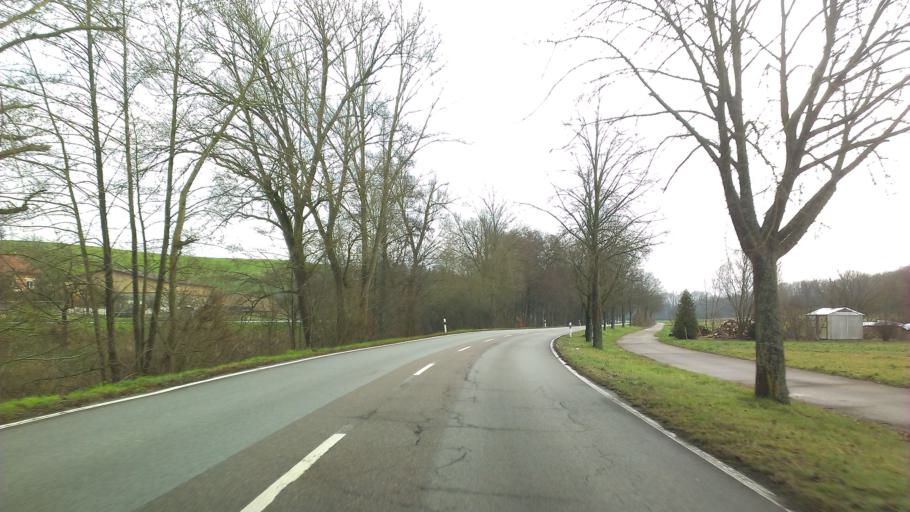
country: DE
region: Baden-Wuerttemberg
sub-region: Karlsruhe Region
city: Balzfeld
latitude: 49.2685
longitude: 8.7935
